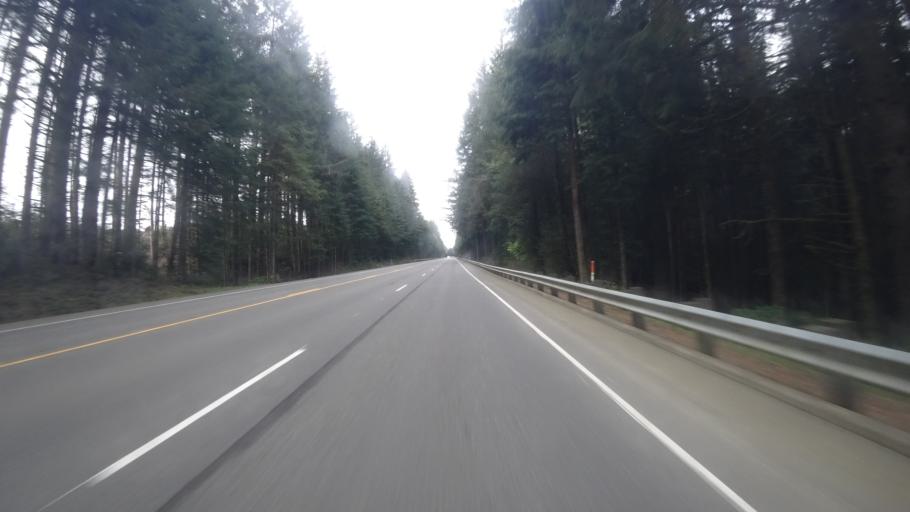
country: US
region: Oregon
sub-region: Coos County
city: Coquille
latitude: 43.2263
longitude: -124.2989
